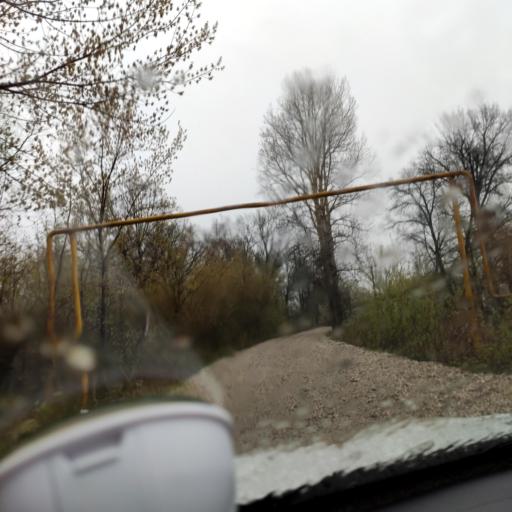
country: RU
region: Samara
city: Novokuybyshevsk
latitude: 53.1417
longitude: 49.9672
